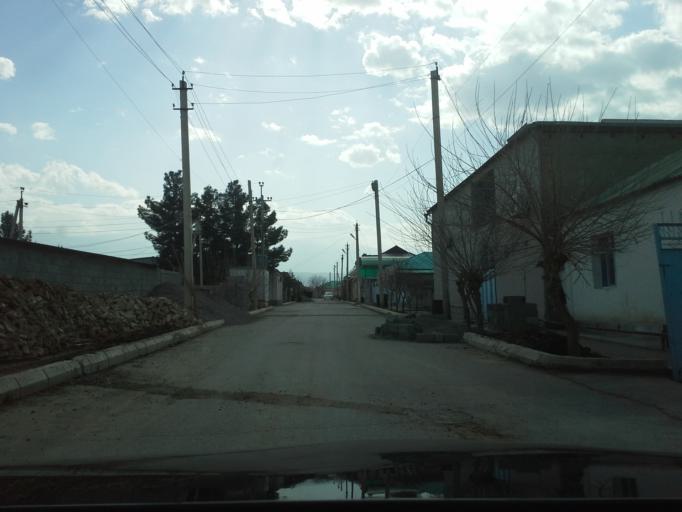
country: TM
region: Ahal
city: Abadan
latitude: 37.9894
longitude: 58.2813
